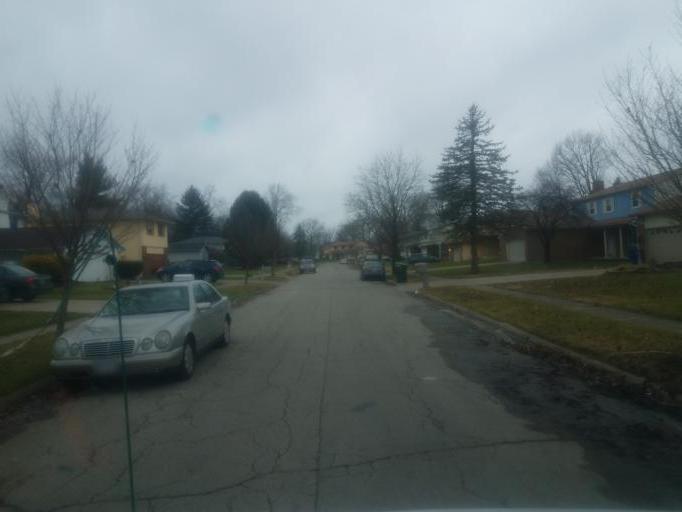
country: US
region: Ohio
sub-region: Franklin County
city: Minerva Park
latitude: 40.0777
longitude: -82.9588
